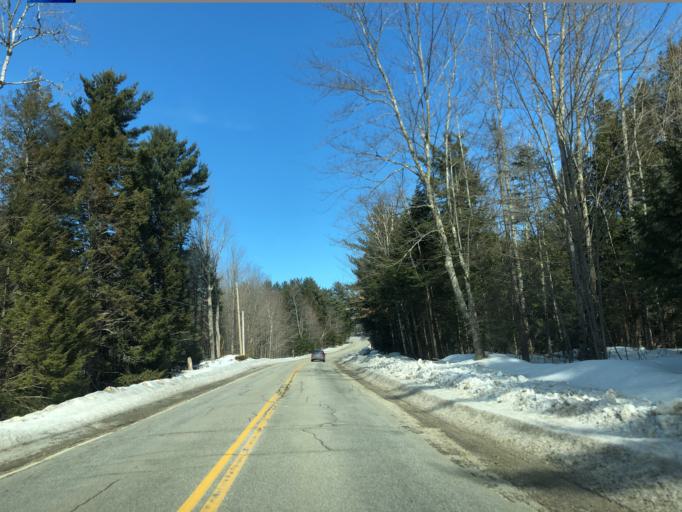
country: US
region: Maine
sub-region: Oxford County
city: Hebron
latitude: 44.2177
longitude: -70.3412
